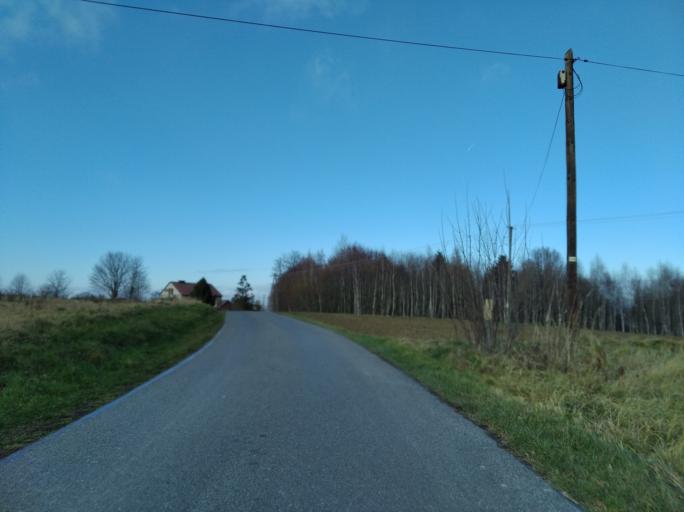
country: PL
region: Subcarpathian Voivodeship
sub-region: Powiat strzyzowski
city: Czudec
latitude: 49.9142
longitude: 21.8459
